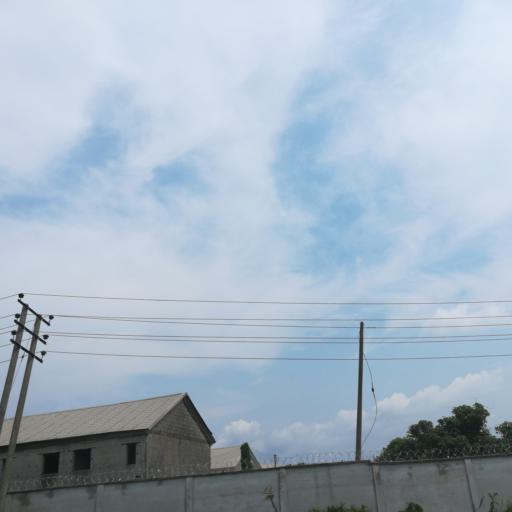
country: NG
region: Rivers
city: Port Harcourt
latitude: 4.8497
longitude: 7.0151
